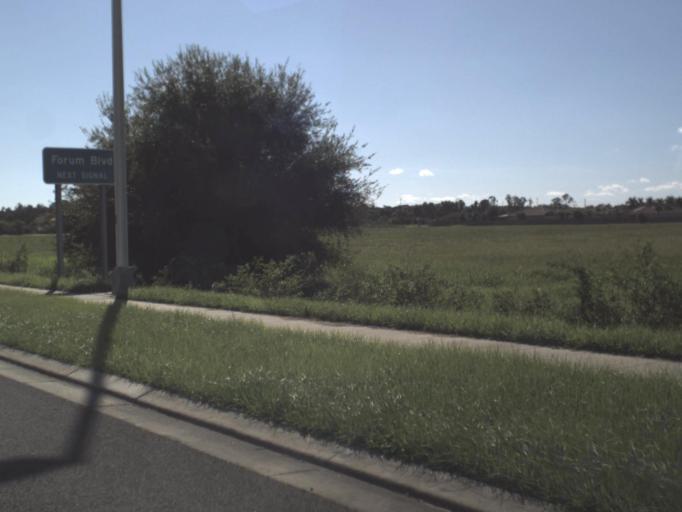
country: US
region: Florida
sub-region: Lee County
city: Fort Myers
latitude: 26.6327
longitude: -81.7960
